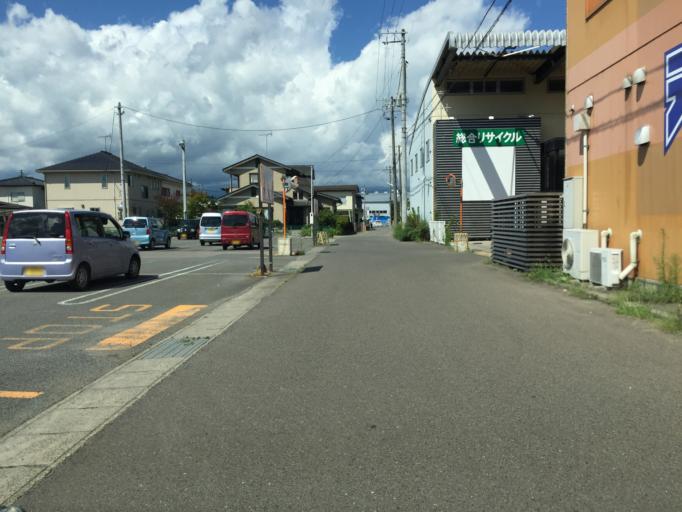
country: JP
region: Fukushima
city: Fukushima-shi
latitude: 37.7267
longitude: 140.4617
